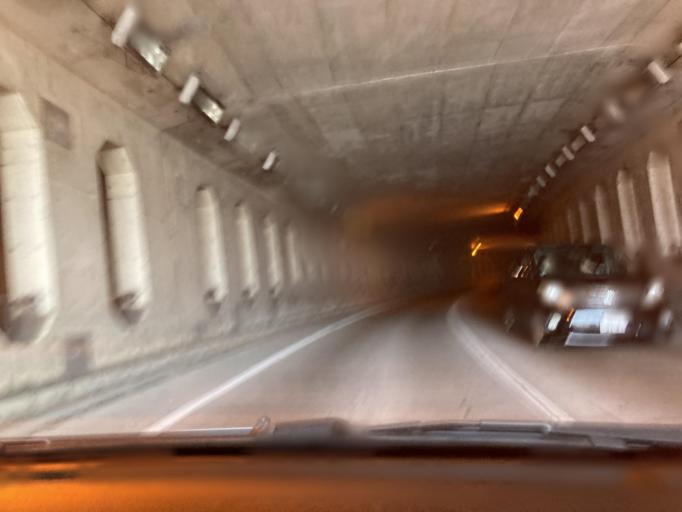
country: JP
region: Okinawa
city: Tomigusuku
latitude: 26.1851
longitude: 127.6740
